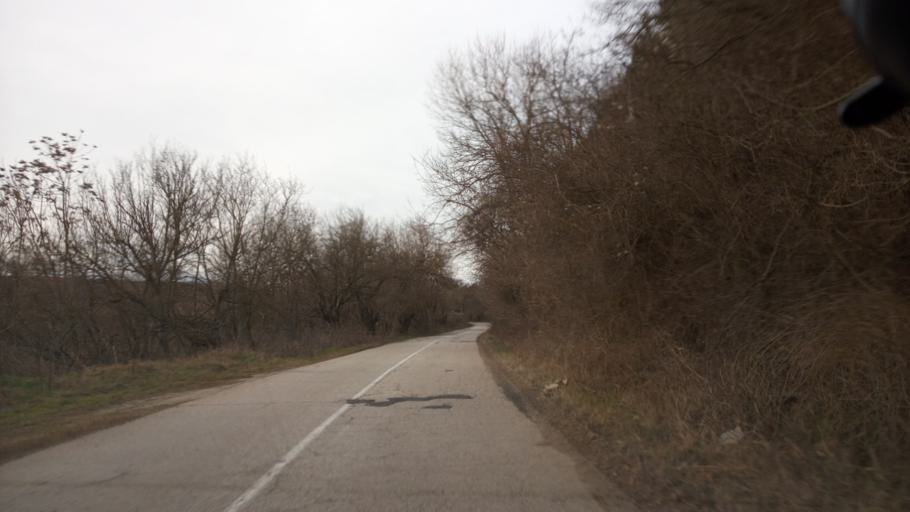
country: BG
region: Pleven
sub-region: Obshtina Belene
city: Belene
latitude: 43.6168
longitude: 25.0293
